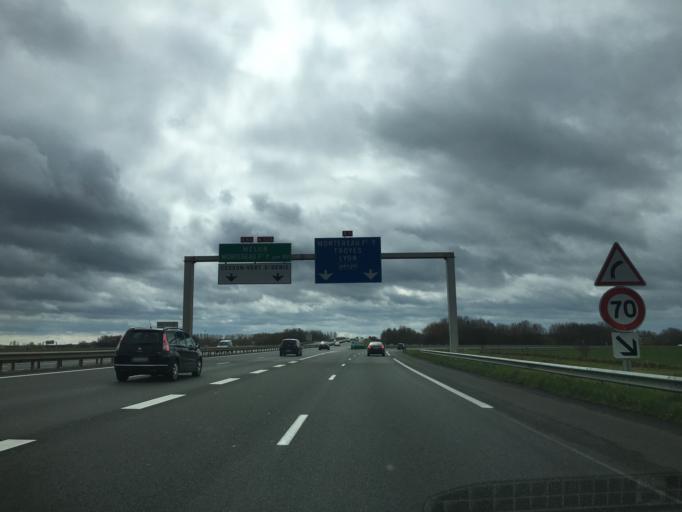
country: FR
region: Ile-de-France
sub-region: Departement de Seine-et-Marne
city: Vert-Saint-Denis
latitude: 48.5998
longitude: 2.6344
